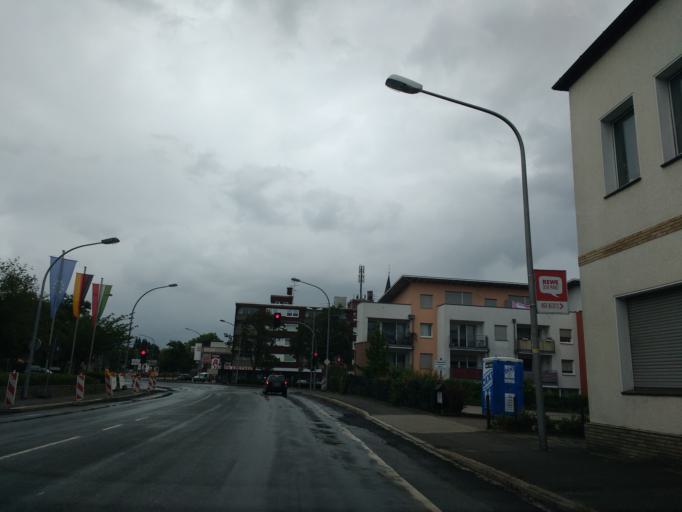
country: DE
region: North Rhine-Westphalia
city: Lengerich
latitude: 52.1912
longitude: 7.8476
